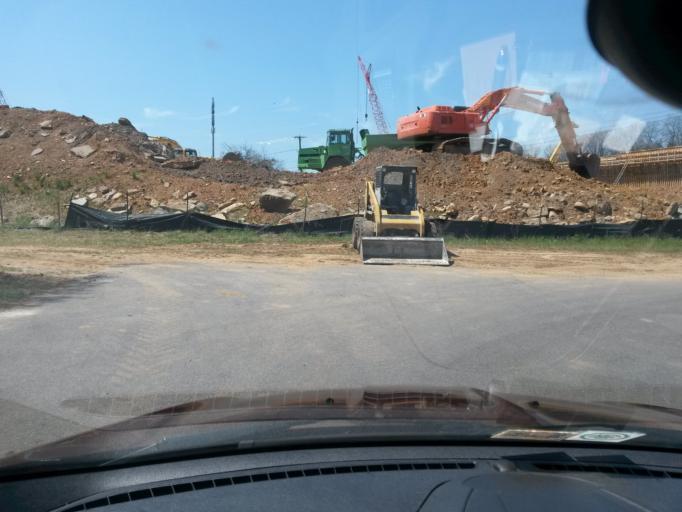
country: US
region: Virginia
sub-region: City of Roanoke
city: Cedar Bluff
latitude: 37.2567
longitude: -79.9471
